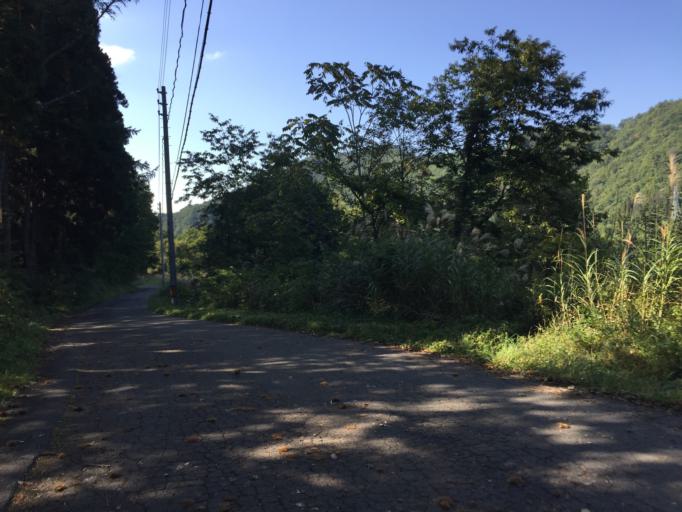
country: JP
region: Yamagata
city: Yonezawa
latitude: 37.8430
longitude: 140.1940
